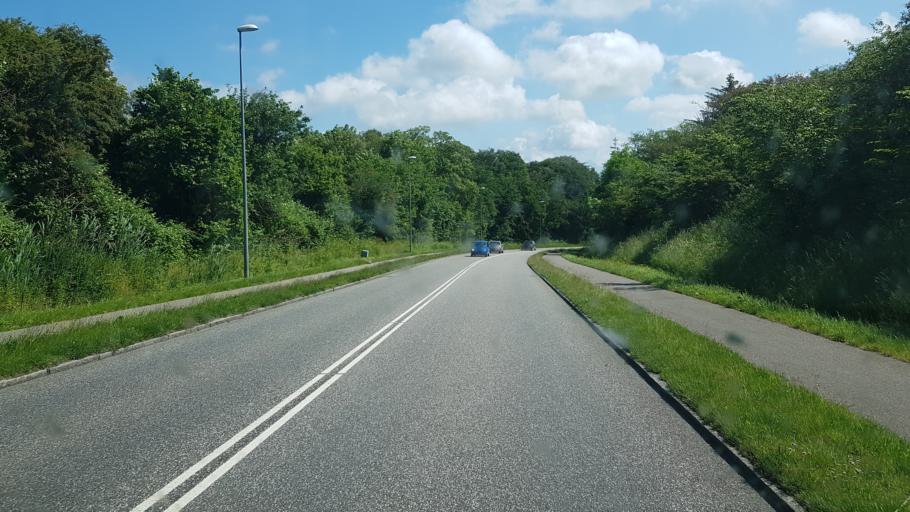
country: DK
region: Central Jutland
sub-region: Lemvig Kommune
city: Lemvig
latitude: 56.5404
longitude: 8.3080
